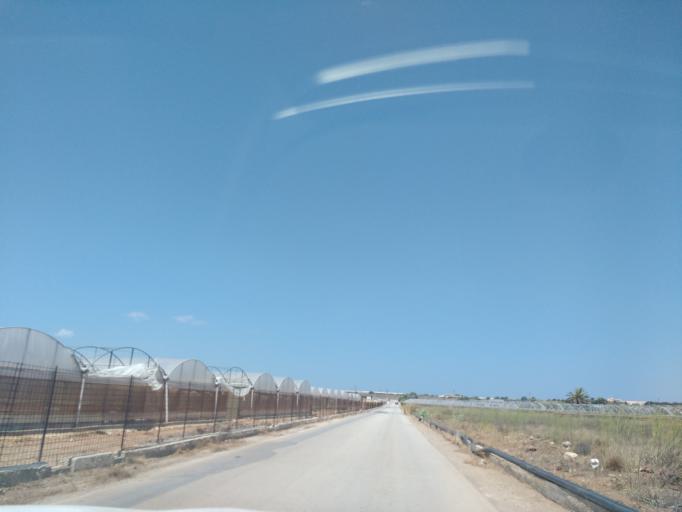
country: IT
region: Sicily
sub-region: Provincia di Siracusa
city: Pachino
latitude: 36.6704
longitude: 15.0833
